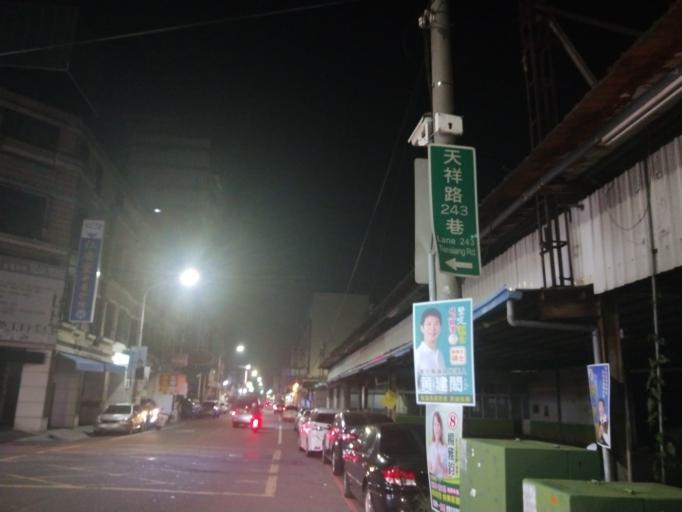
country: TW
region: Taiwan
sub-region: Changhua
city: Chang-hua
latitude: 24.0634
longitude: 120.5334
